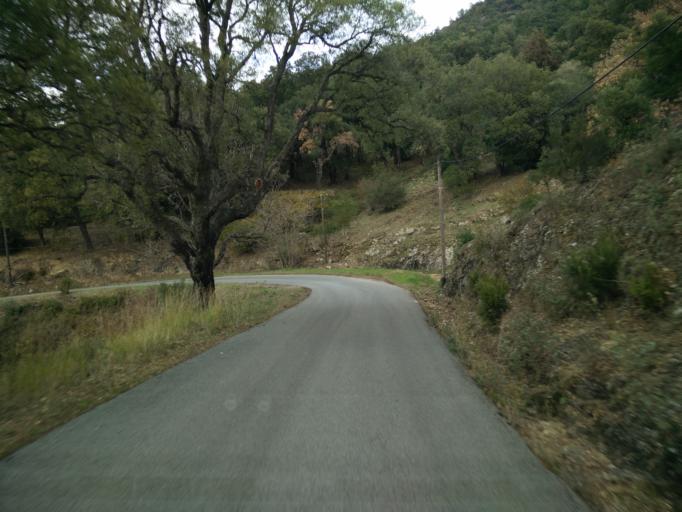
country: FR
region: Provence-Alpes-Cote d'Azur
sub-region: Departement du Var
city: Le Plan-de-la-Tour
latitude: 43.3688
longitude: 6.5996
